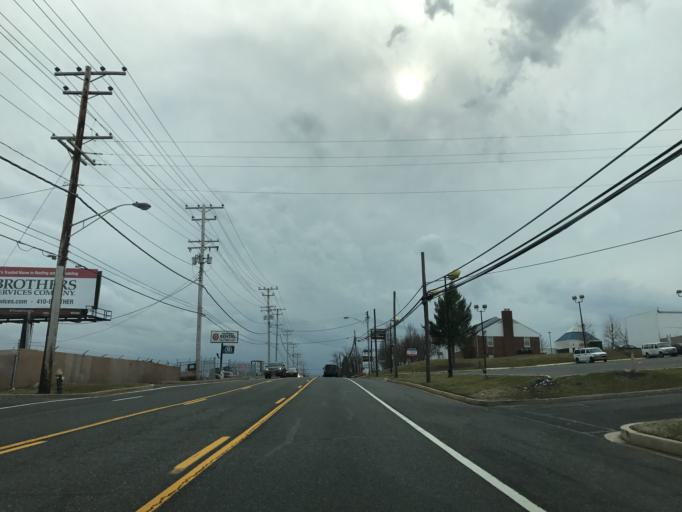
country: US
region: Maryland
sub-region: Harford County
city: Bel Air
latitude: 39.5216
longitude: -76.3592
